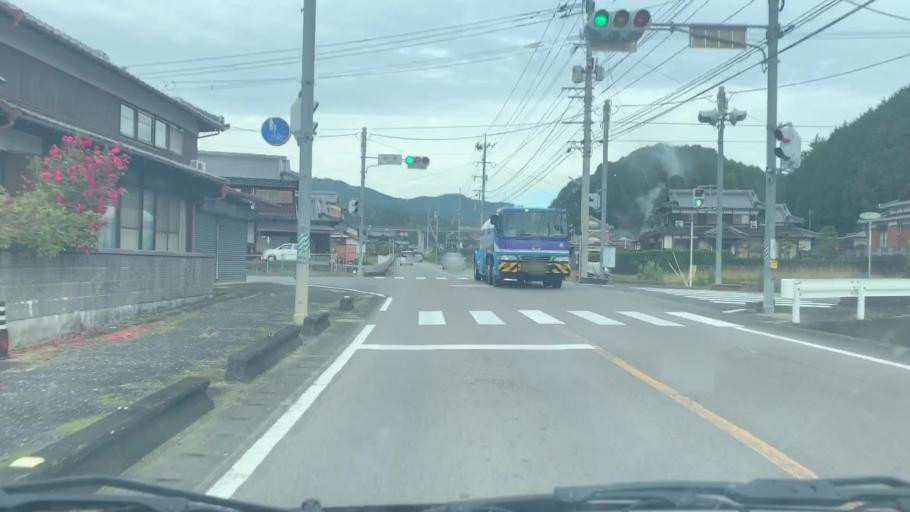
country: JP
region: Saga Prefecture
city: Ureshinomachi-shimojuku
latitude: 33.1399
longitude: 129.9784
